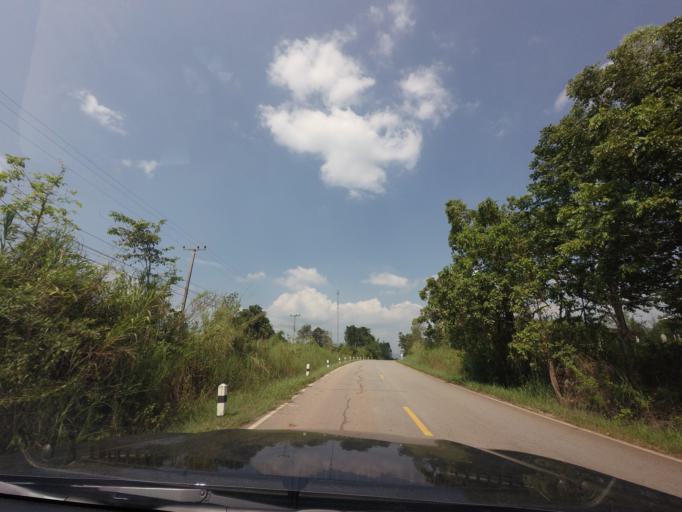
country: TH
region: Uttaradit
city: Ban Khok
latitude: 17.9705
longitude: 101.0211
